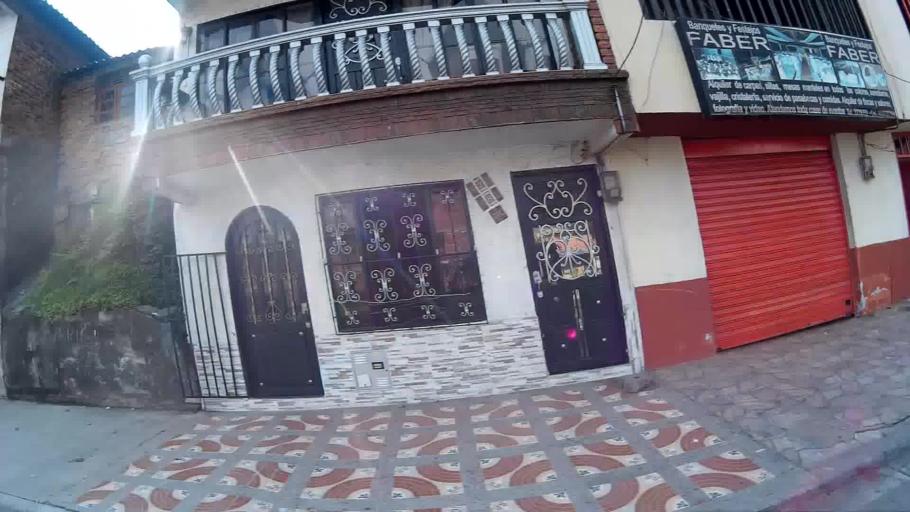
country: CO
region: Risaralda
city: Pereira
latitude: 4.8051
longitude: -75.7366
